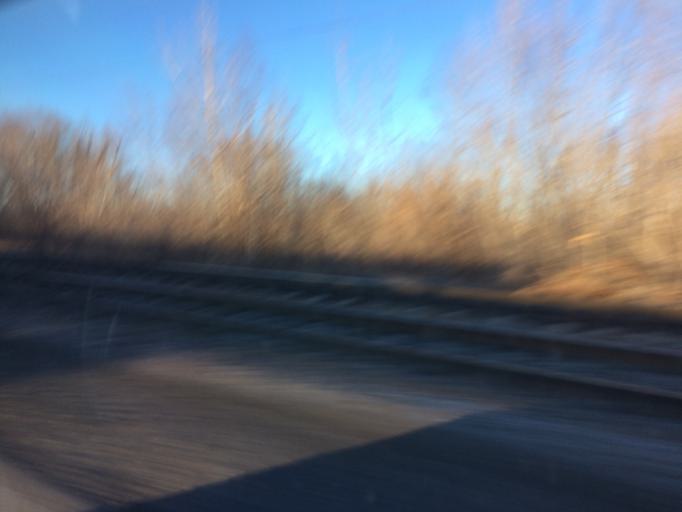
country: RU
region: Chelyabinsk
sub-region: Gorod Magnitogorsk
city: Magnitogorsk
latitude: 53.4071
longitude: 59.0299
